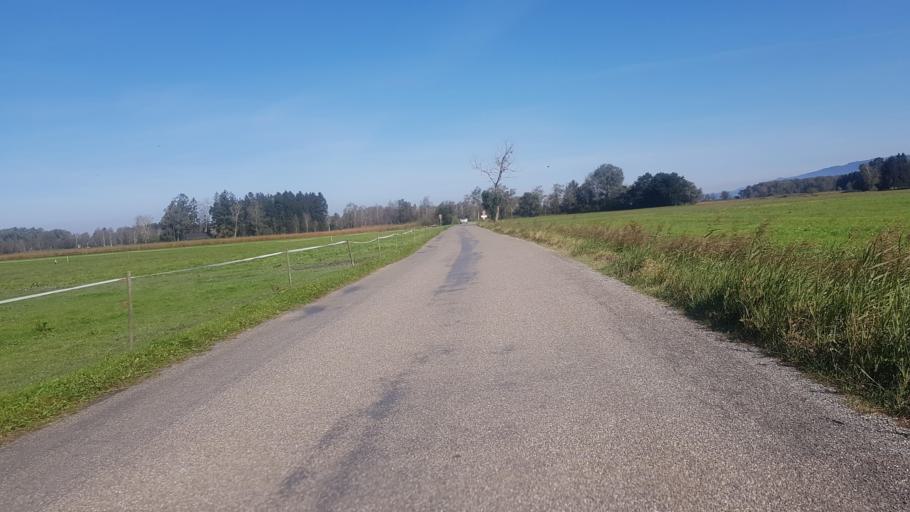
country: AT
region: Vorarlberg
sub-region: Politischer Bezirk Bregenz
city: Gaissau
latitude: 47.4850
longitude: 9.6241
